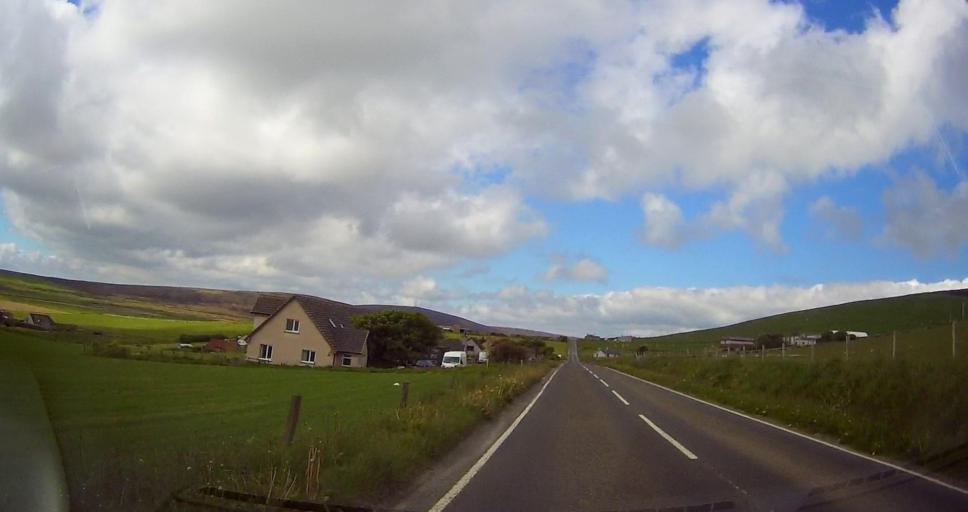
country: GB
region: Scotland
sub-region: Orkney Islands
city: Orkney
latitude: 58.9782
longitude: -3.0128
